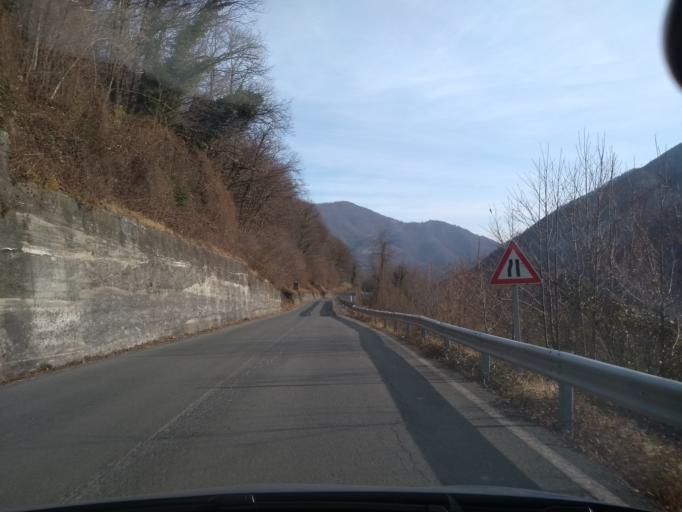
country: IT
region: Piedmont
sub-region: Provincia di Torino
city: Ceres
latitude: 45.3204
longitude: 7.3606
